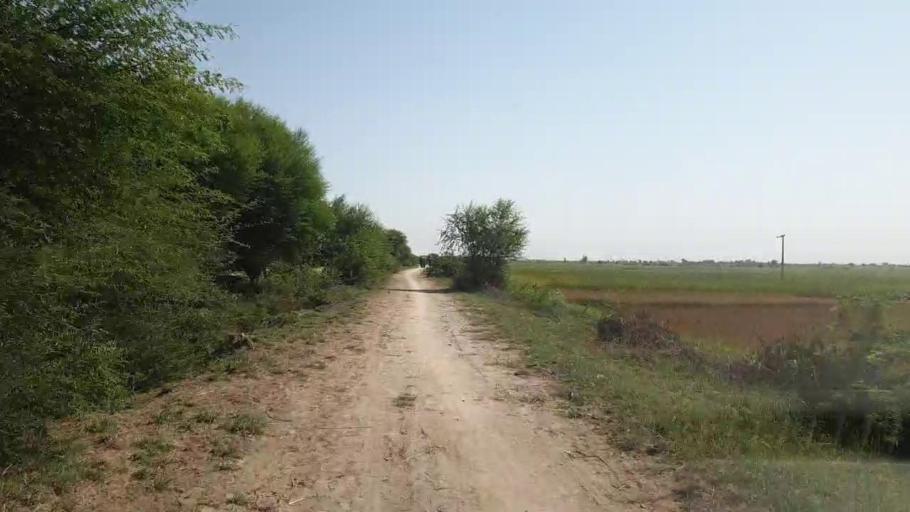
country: PK
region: Sindh
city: Kadhan
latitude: 24.6084
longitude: 69.0007
